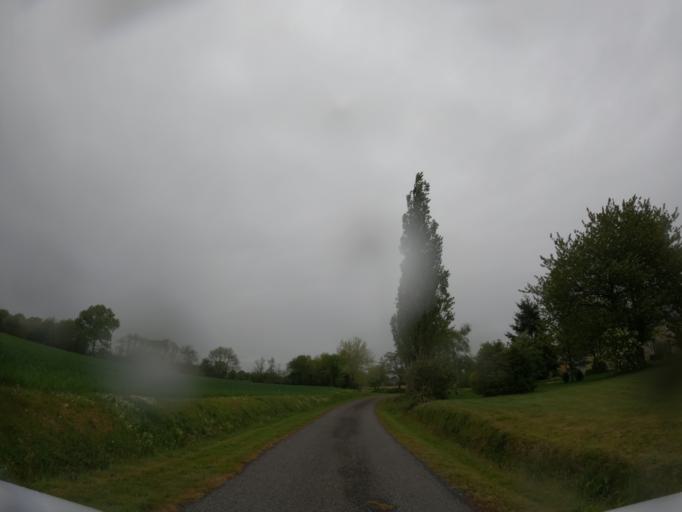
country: FR
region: Pays de la Loire
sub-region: Departement de la Mayenne
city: Ballots
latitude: 47.9471
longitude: -1.1273
